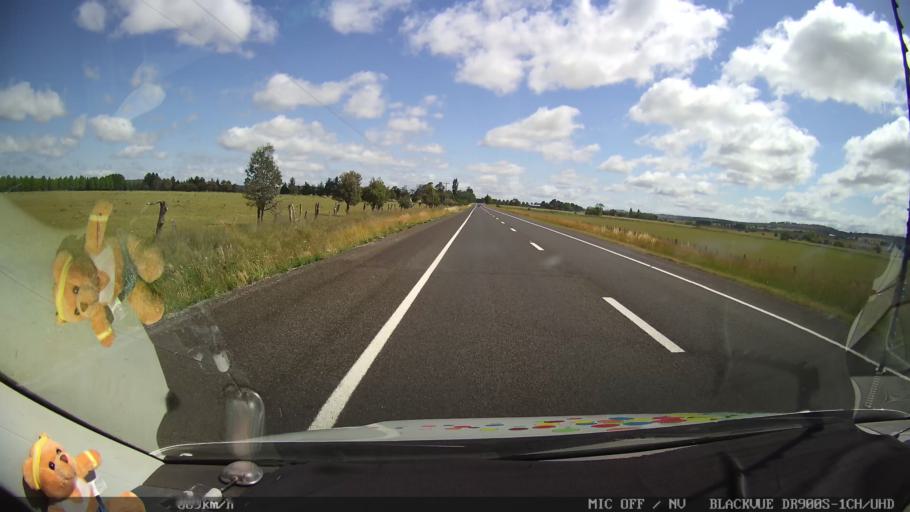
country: AU
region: New South Wales
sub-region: Glen Innes Severn
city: Glen Innes
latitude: -29.8273
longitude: 151.7387
